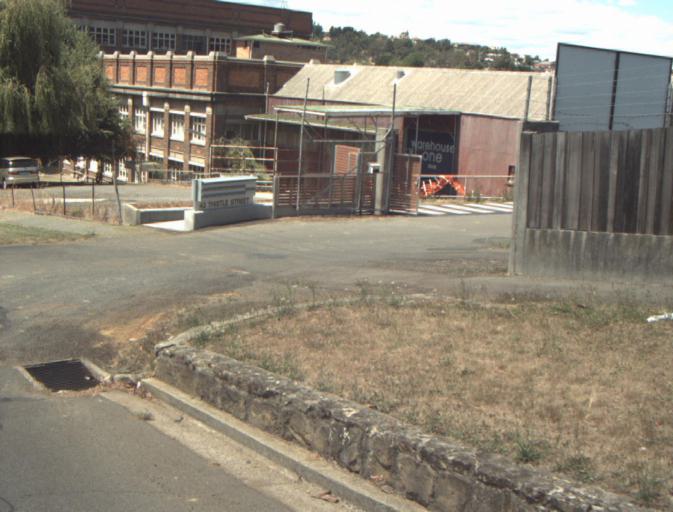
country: AU
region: Tasmania
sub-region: Launceston
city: West Launceston
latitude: -41.4536
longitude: 147.1380
